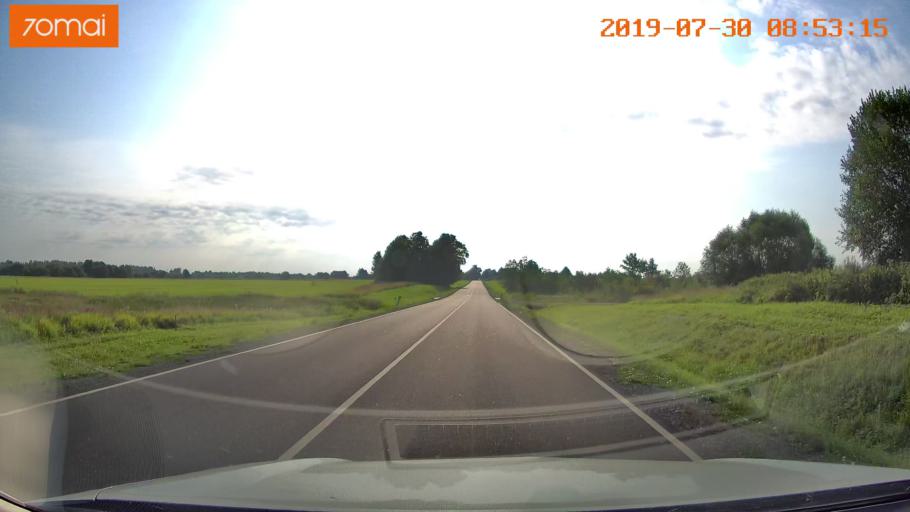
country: RU
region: Kaliningrad
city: Chernyakhovsk
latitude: 54.6019
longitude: 21.9933
